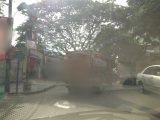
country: IN
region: Karnataka
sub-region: Bangalore Urban
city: Bangalore
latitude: 12.9850
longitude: 77.5453
